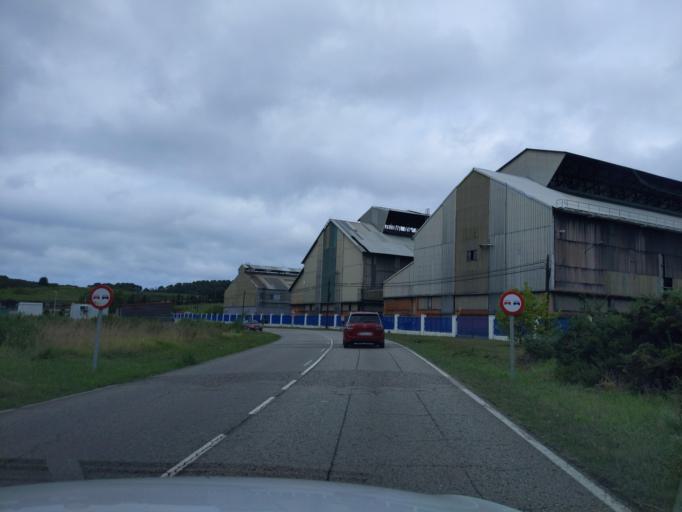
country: ES
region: Asturias
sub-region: Province of Asturias
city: Aviles
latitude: 43.5820
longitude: -5.9152
